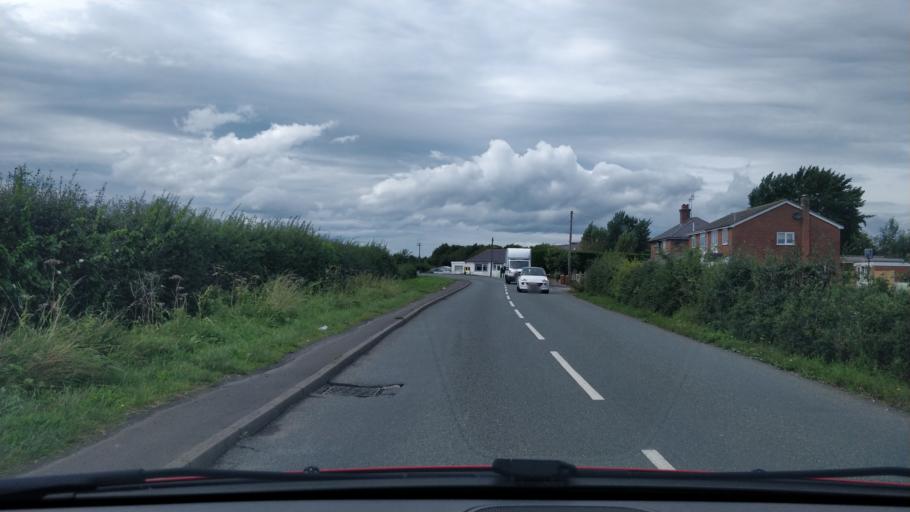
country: GB
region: England
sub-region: Cheshire West and Chester
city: Eccleston
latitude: 53.1545
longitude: -2.9176
